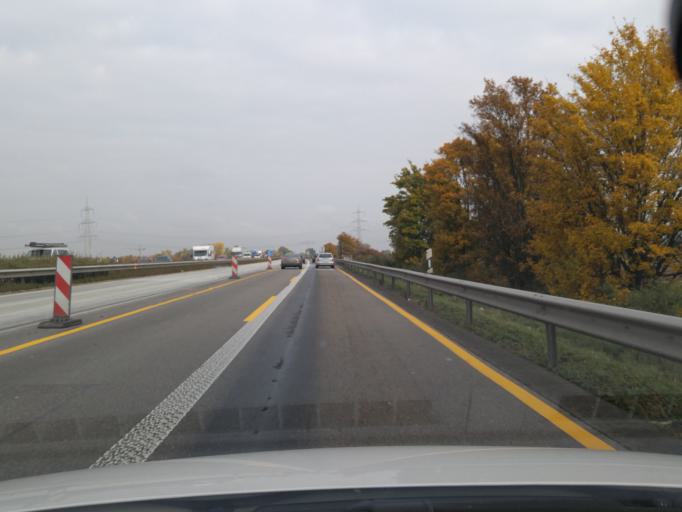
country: DE
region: Rheinland-Pfalz
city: Hessheim
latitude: 49.5324
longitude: 8.3148
